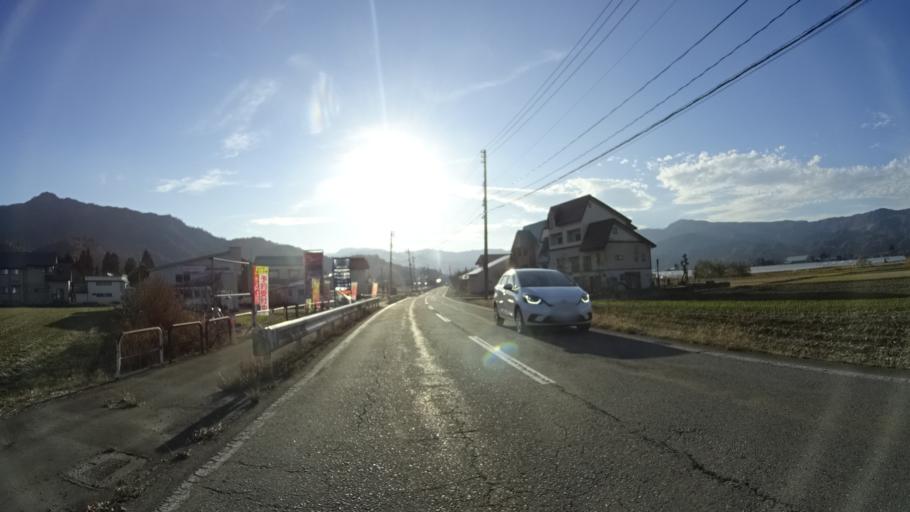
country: JP
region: Niigata
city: Shiozawa
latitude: 37.0118
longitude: 138.8528
